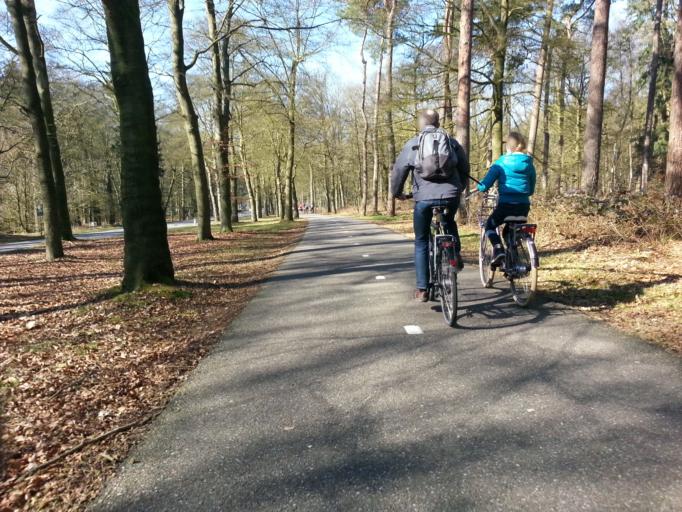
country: NL
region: Utrecht
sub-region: Gemeente Utrechtse Heuvelrug
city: Doorn
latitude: 52.0316
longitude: 5.3731
